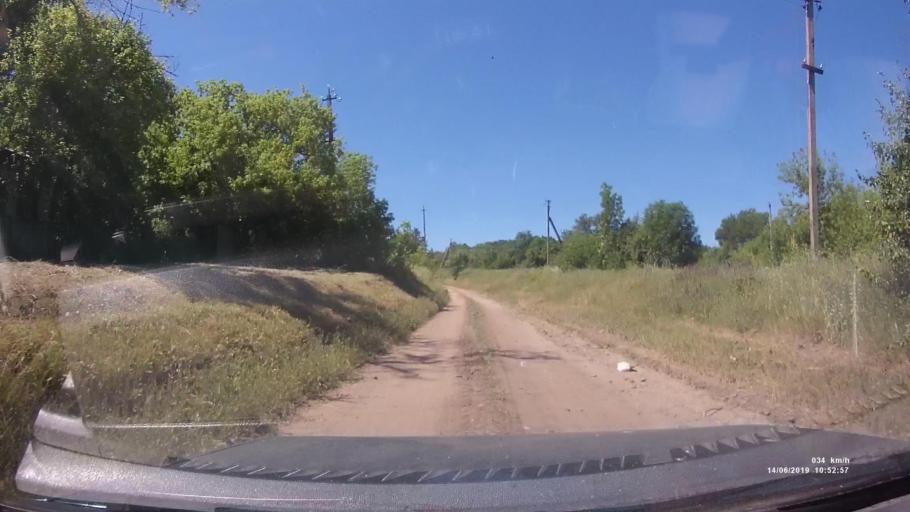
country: RU
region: Rostov
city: Kazanskaya
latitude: 49.8645
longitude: 41.3838
